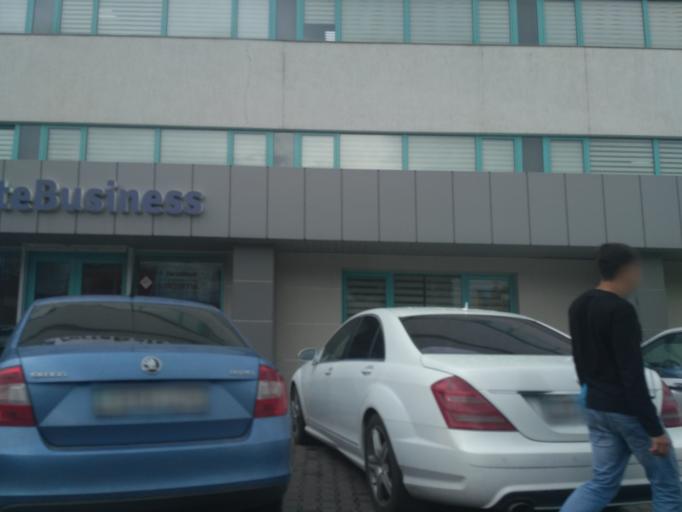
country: KZ
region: Almaty Oblysy
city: Burunday
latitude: 43.2017
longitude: 76.6264
